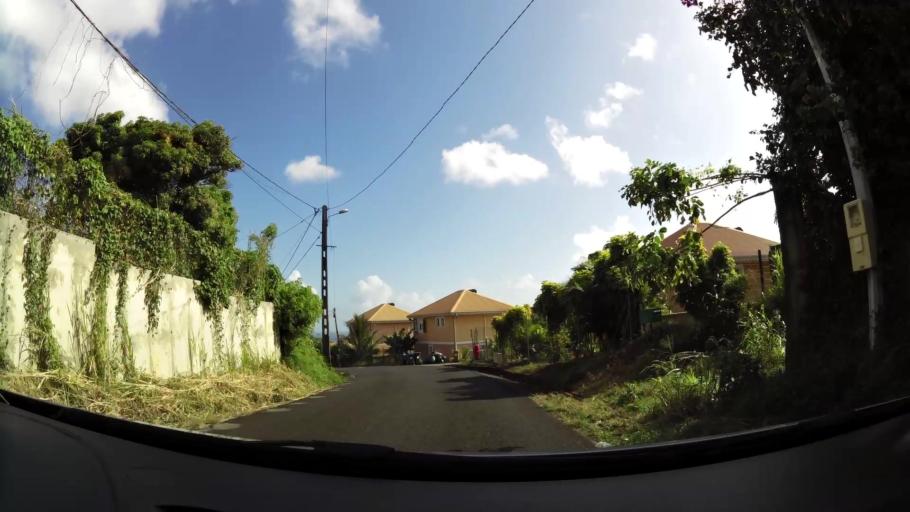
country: MQ
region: Martinique
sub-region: Martinique
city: La Trinite
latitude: 14.7348
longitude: -60.9747
